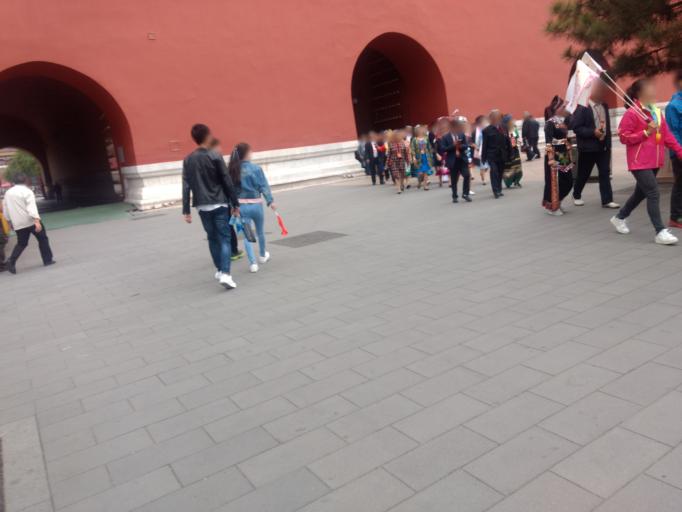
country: CN
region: Beijing
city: Beijing
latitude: 39.9087
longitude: 116.3910
